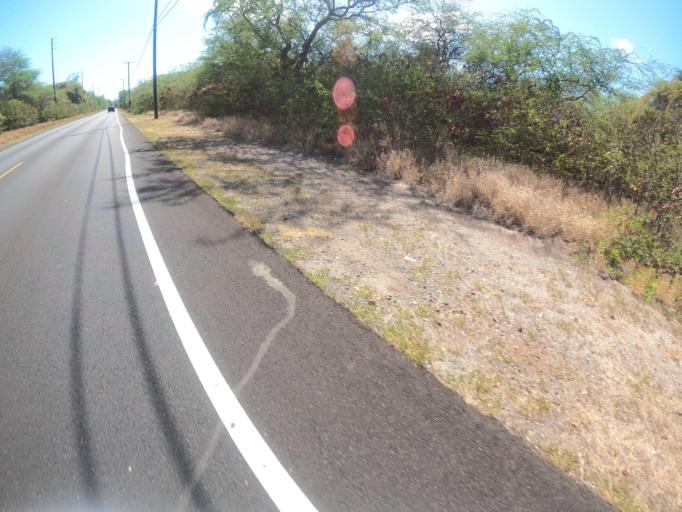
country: US
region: Hawaii
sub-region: Honolulu County
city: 'Ewa Villages
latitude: 21.3080
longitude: -158.0565
